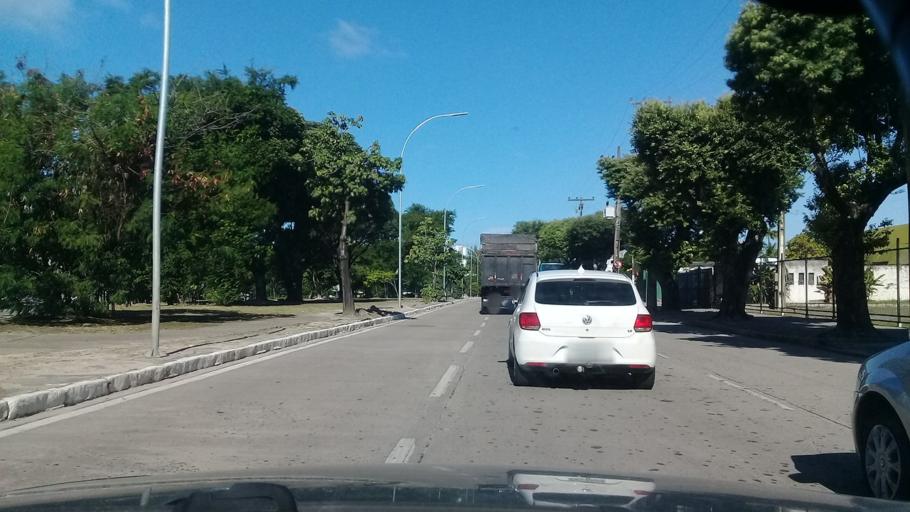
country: BR
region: Pernambuco
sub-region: Recife
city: Recife
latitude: -8.1225
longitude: -34.9172
